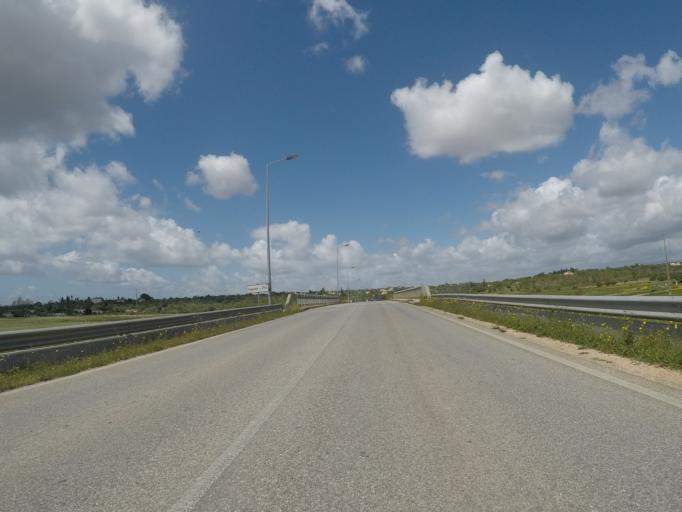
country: PT
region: Faro
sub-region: Silves
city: Armacao de Pera
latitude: 37.1155
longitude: -8.3432
